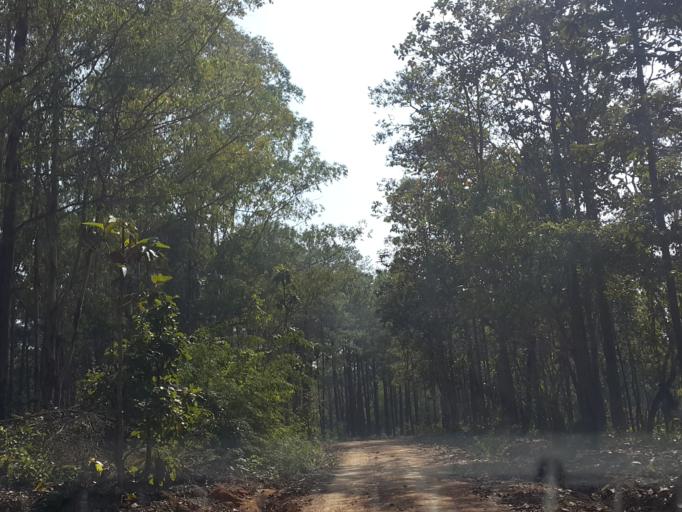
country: TH
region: Chiang Mai
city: Hot
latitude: 18.1487
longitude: 98.4316
